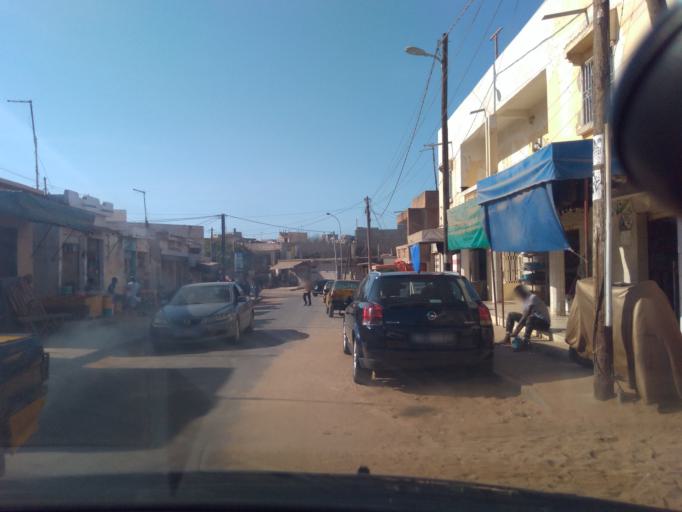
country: SN
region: Dakar
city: Pikine
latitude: 14.7582
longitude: -17.4311
